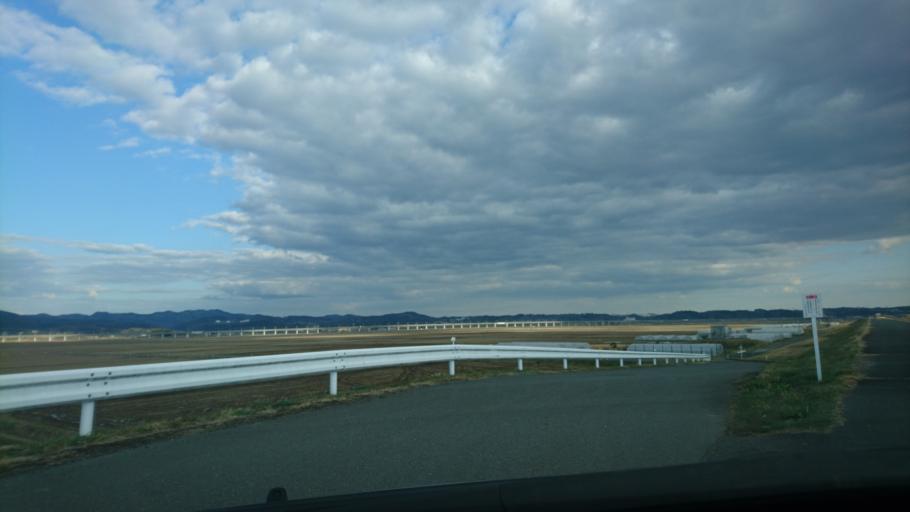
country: JP
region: Iwate
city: Ichinoseki
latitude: 38.9601
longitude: 141.1298
